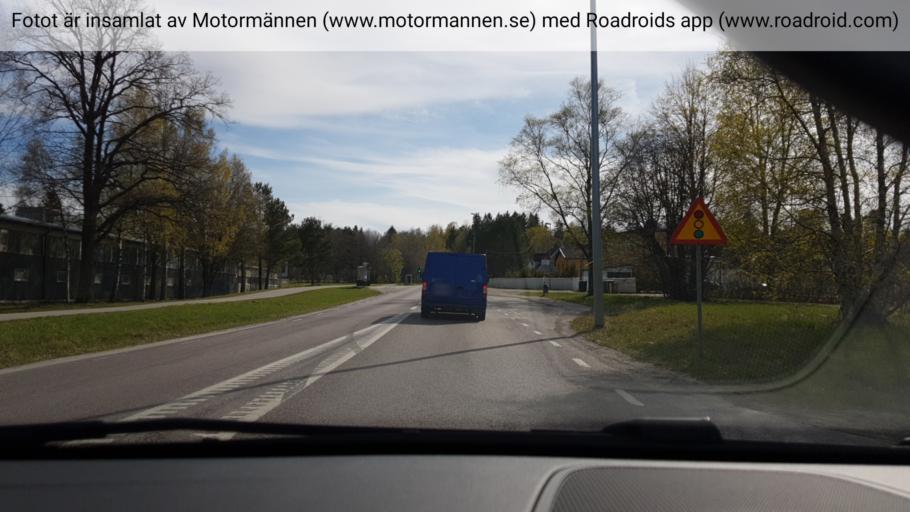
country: SE
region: Stockholm
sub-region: Botkyrka Kommun
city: Tumba
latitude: 59.1891
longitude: 17.8204
